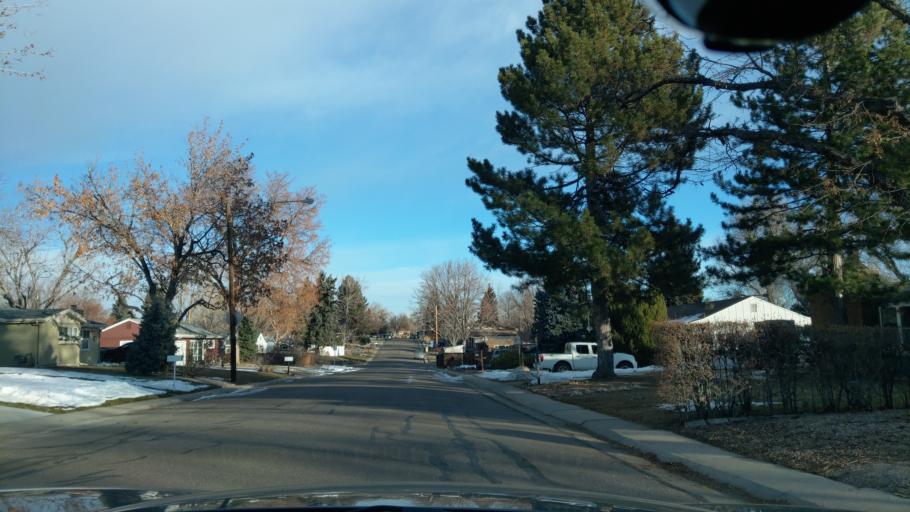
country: US
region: Colorado
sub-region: Jefferson County
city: Lakewood
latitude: 39.7297
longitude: -105.1139
